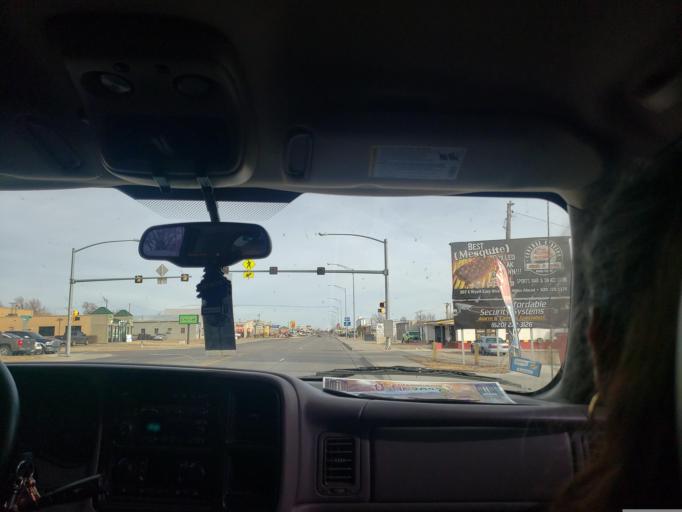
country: US
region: Kansas
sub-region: Ford County
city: Dodge City
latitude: 37.7541
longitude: -100.0414
